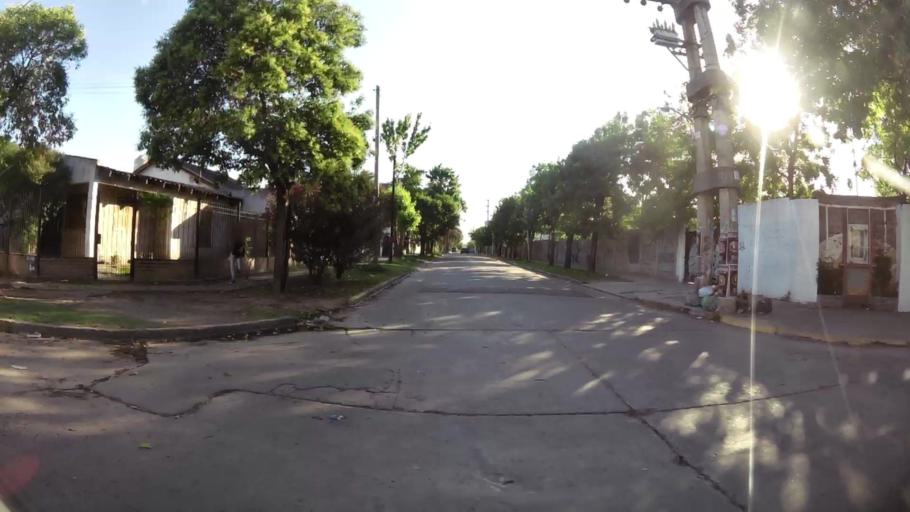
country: AR
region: Buenos Aires
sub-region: Partido de Merlo
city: Merlo
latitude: -34.6874
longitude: -58.7310
